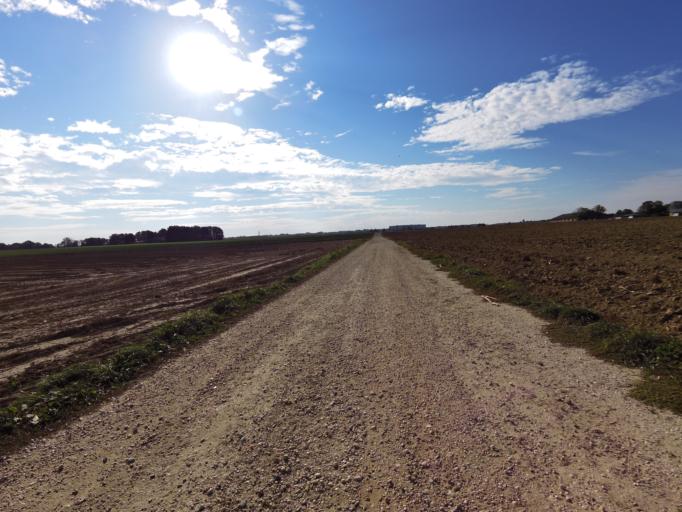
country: NL
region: Limburg
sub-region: Gemeente Onderbanken
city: Schinveld
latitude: 50.9704
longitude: 5.9596
